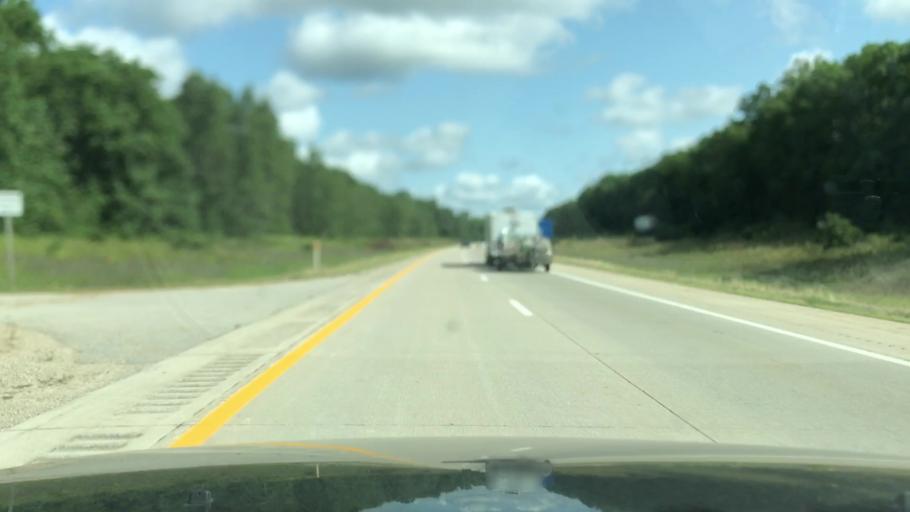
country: US
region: Michigan
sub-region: Montcalm County
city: Howard City
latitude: 43.3819
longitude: -85.5179
